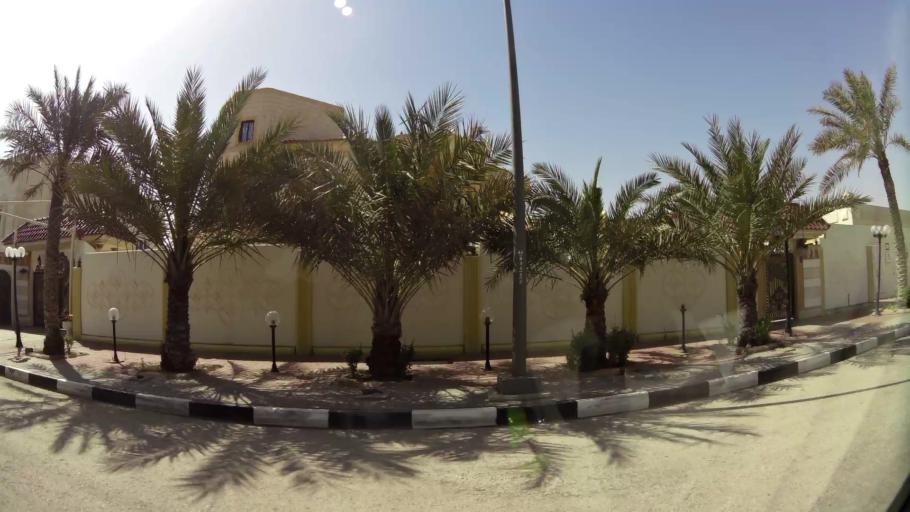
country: QA
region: Baladiyat ad Dawhah
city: Doha
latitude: 25.3640
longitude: 51.4968
